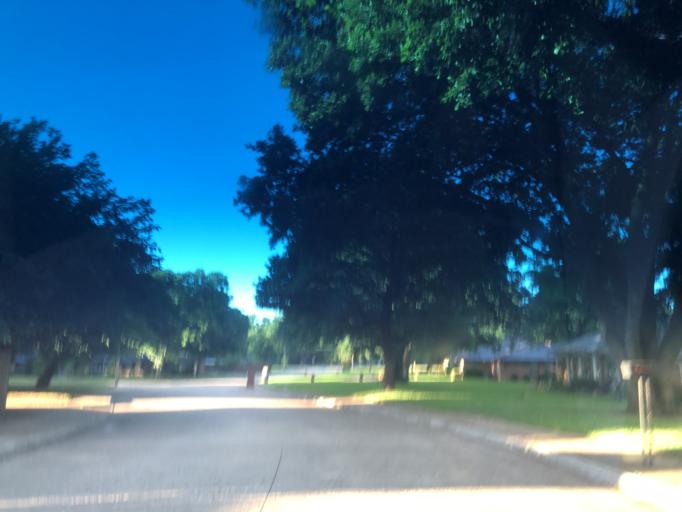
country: US
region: Texas
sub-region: Dallas County
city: Grand Prairie
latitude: 32.7813
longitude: -97.0347
